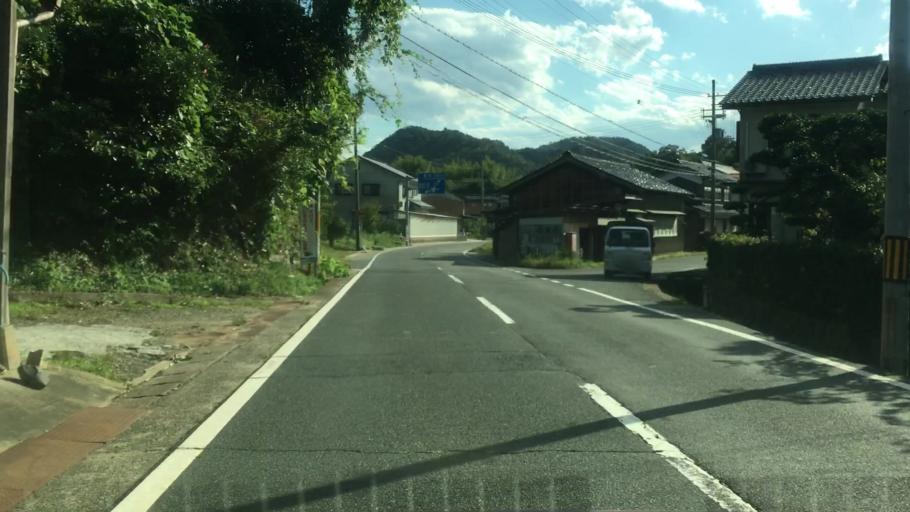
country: JP
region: Hyogo
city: Toyooka
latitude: 35.6374
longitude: 134.9421
